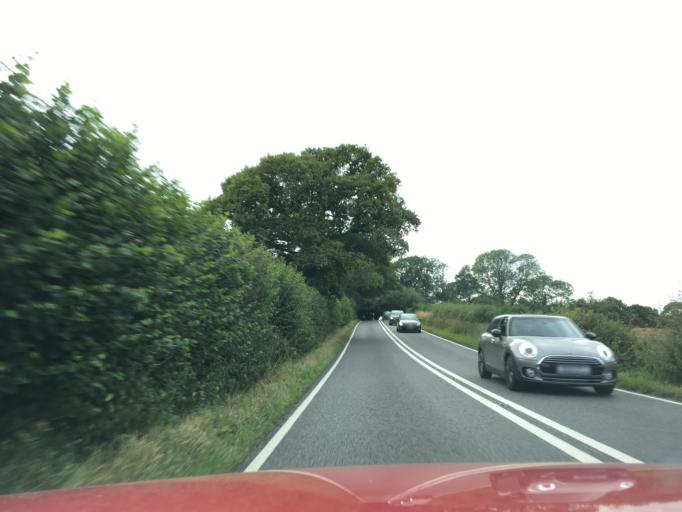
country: GB
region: England
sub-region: Hampshire
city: Swanmore
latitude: 51.0433
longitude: -1.1705
